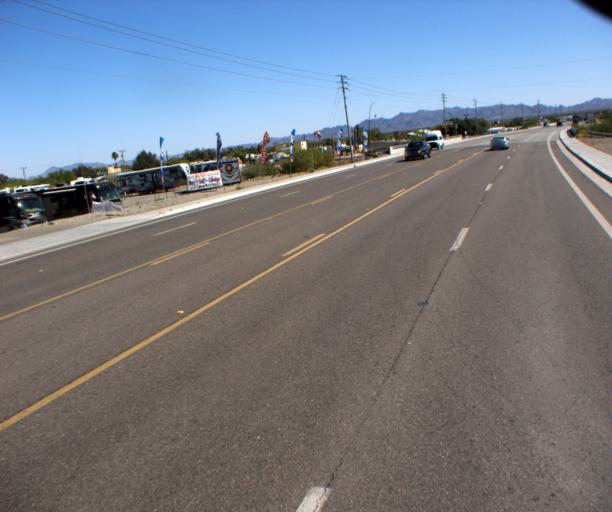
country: US
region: Arizona
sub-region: La Paz County
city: Quartzsite
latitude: 33.6653
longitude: -114.2257
